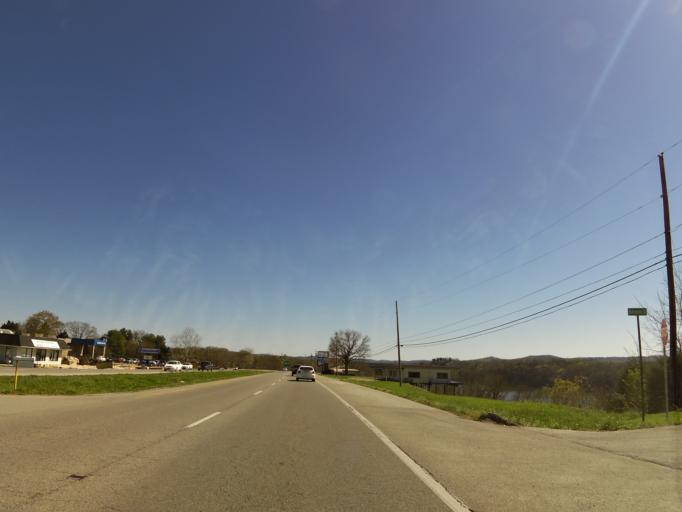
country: US
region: Kentucky
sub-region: Pulaski County
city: Somerset
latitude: 37.0129
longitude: -84.6272
